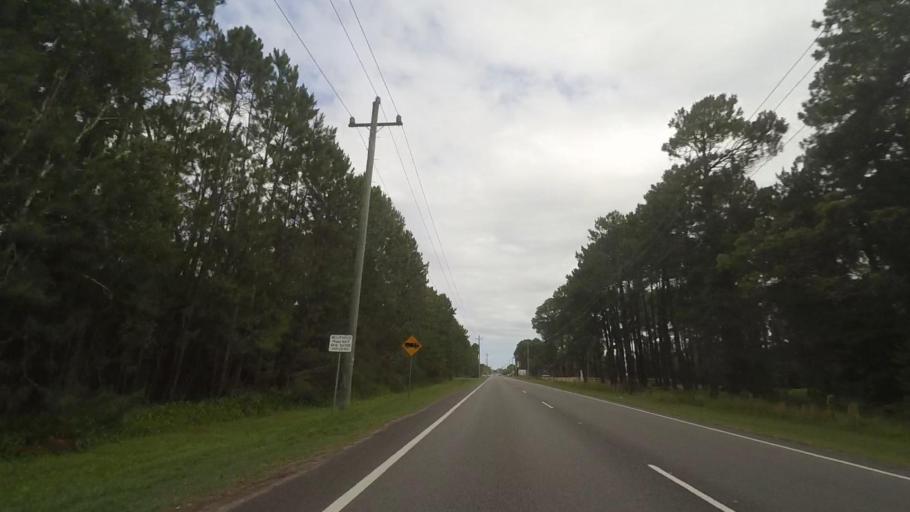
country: AU
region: New South Wales
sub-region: Great Lakes
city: Hawks Nest
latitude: -32.6480
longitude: 152.1477
